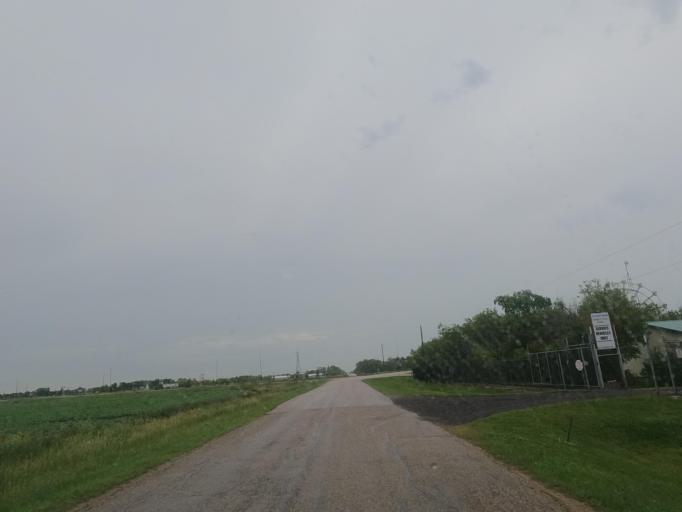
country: CA
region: Manitoba
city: Winnipeg
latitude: 49.8367
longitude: -96.9812
